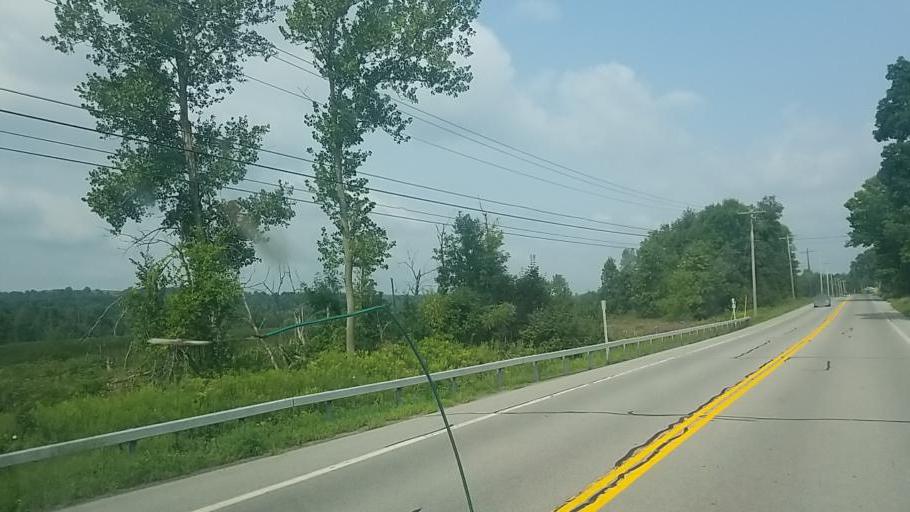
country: US
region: New York
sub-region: Montgomery County
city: Fort Plain
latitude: 42.9725
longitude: -74.6322
